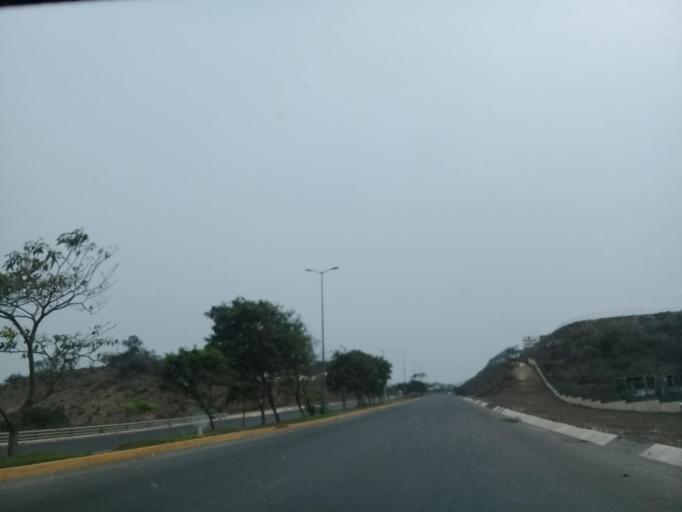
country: MX
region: Veracruz
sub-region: Veracruz
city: Colonia el Renacimiento
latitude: 19.2216
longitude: -96.2202
